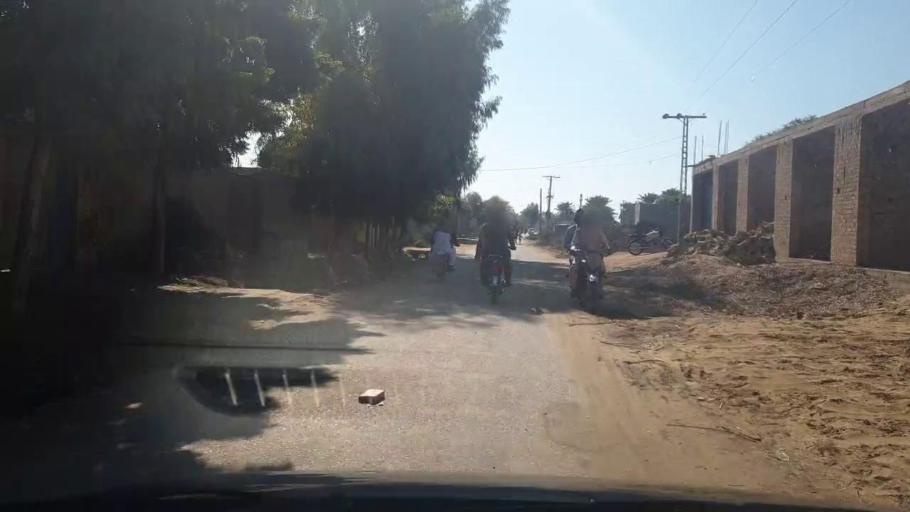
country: PK
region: Sindh
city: Bozdar
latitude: 27.0927
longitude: 68.6248
